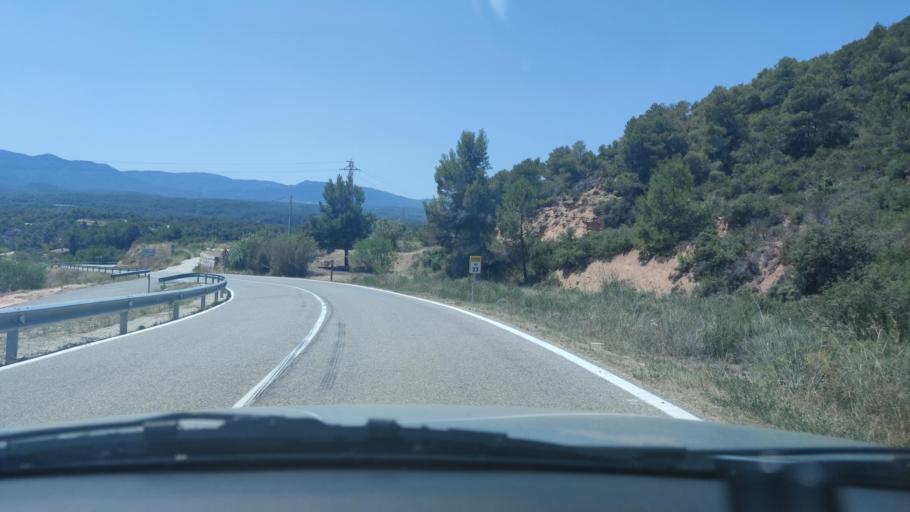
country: ES
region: Catalonia
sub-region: Provincia de Lleida
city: Vinaixa
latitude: 41.4237
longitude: 1.0175
